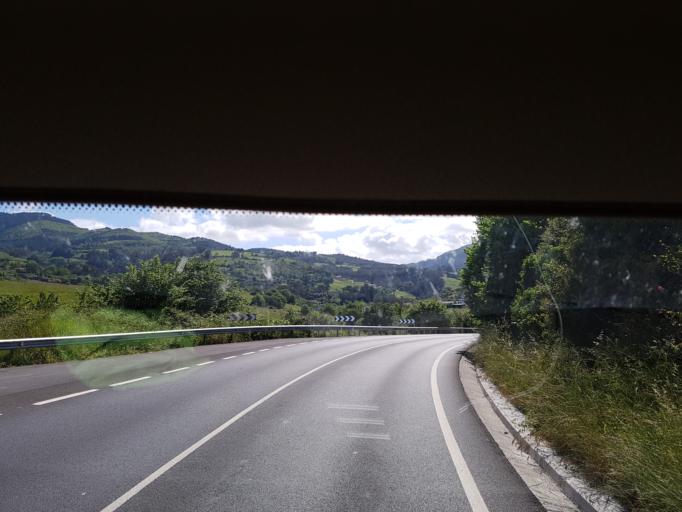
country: ES
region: Basque Country
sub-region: Bizkaia
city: San Julian de Muskiz
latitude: 43.3193
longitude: -3.0844
